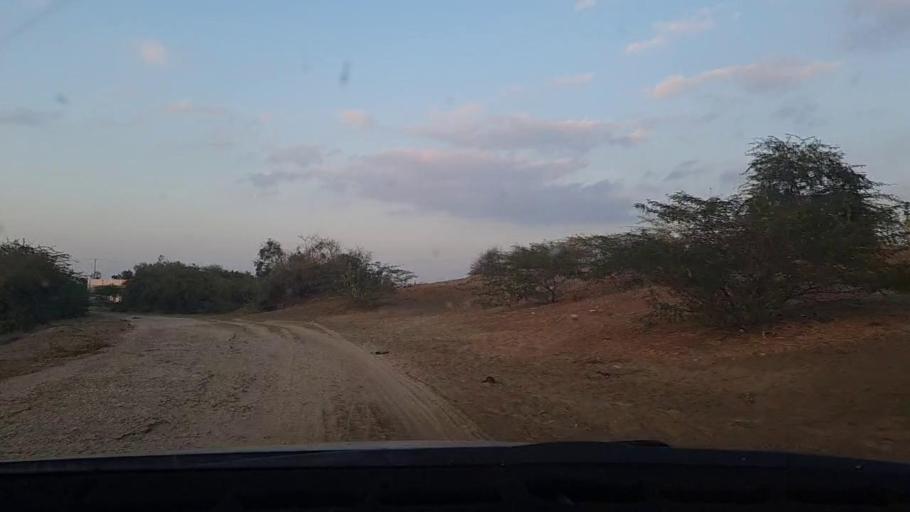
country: PK
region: Sindh
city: Tando Mittha Khan
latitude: 25.9414
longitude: 69.3384
